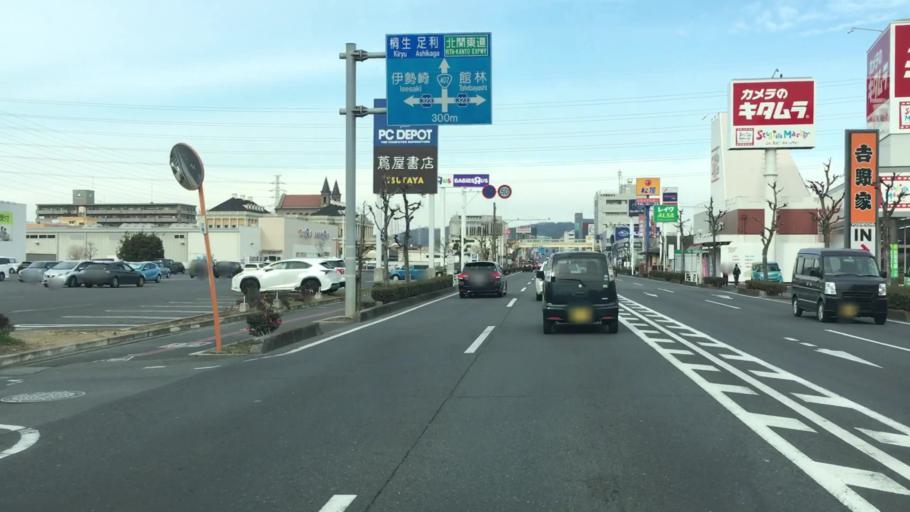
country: JP
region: Gunma
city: Ota
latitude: 36.2814
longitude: 139.3771
